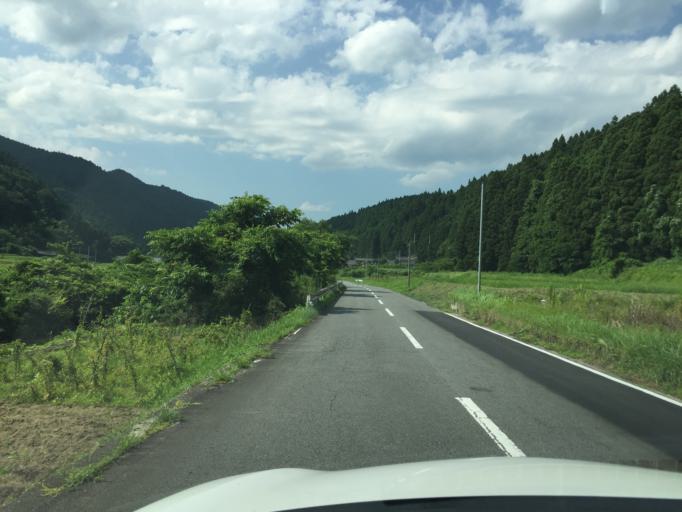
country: JP
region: Fukushima
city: Iwaki
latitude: 37.0185
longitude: 140.7063
